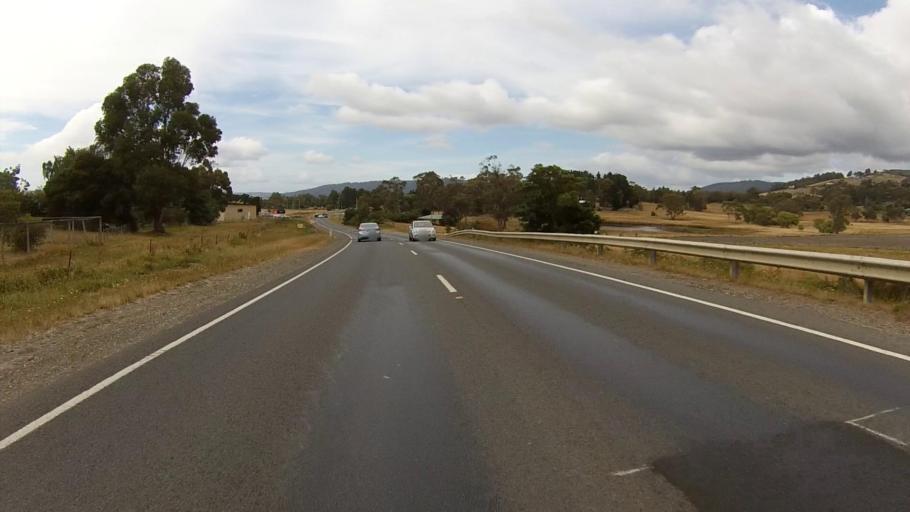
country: AU
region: Tasmania
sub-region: Kingborough
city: Margate
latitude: -43.0313
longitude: 147.2650
